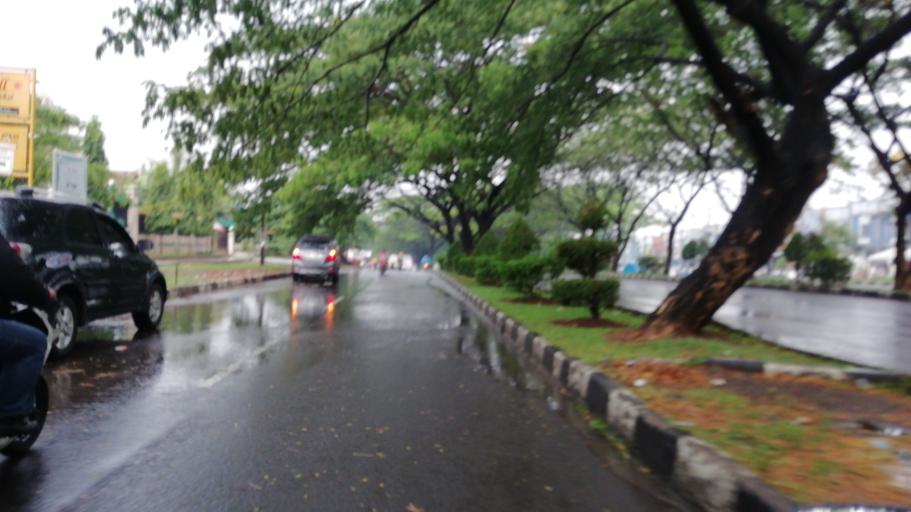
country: ID
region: West Java
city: Cibinong
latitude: -6.4819
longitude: 106.8118
